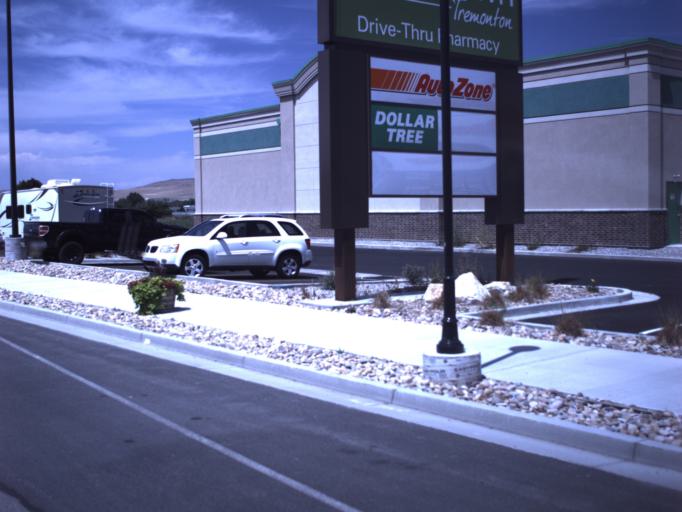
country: US
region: Utah
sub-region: Box Elder County
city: Tremonton
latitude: 41.7117
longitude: -112.1719
